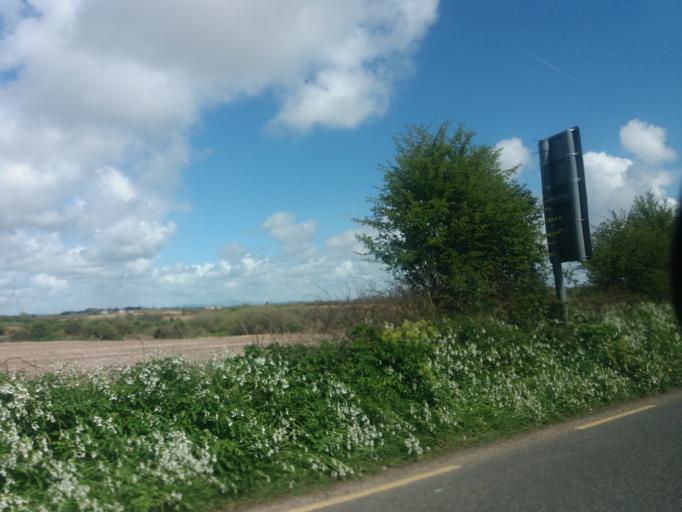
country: IE
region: Munster
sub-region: Waterford
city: Dunmore East
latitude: 52.2473
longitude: -6.8585
